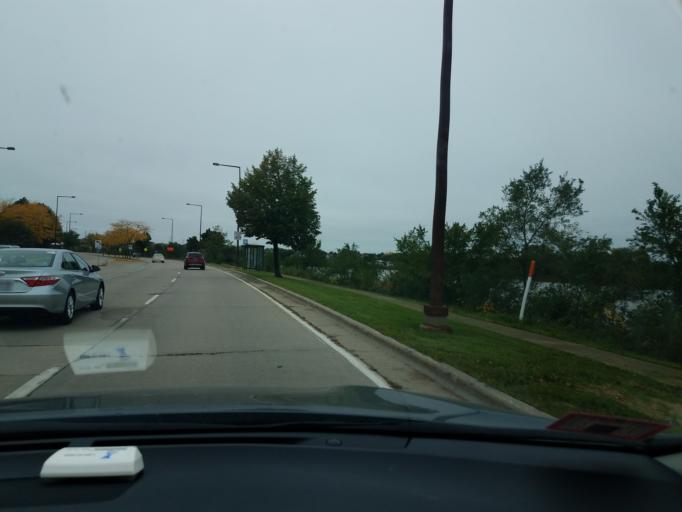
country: US
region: Illinois
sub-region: Cook County
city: Wheeling
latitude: 42.1685
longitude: -87.9286
